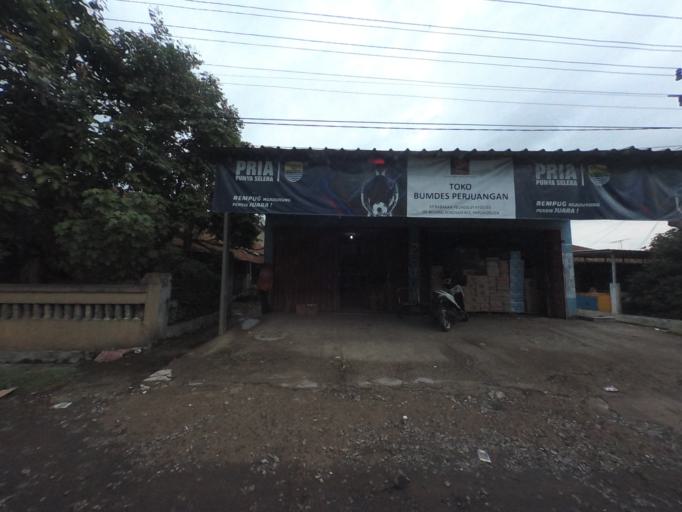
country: ID
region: West Java
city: Cicurug
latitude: -6.8358
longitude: 106.7603
